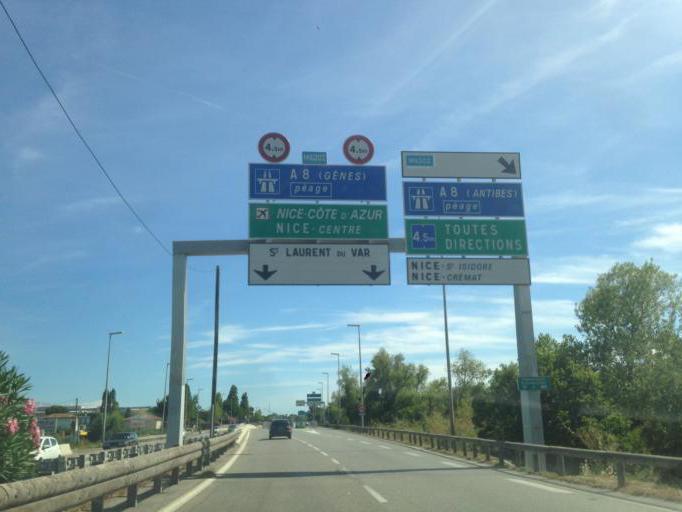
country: FR
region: Provence-Alpes-Cote d'Azur
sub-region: Departement des Alpes-Maritimes
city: La Gaude
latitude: 43.7130
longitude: 7.1873
